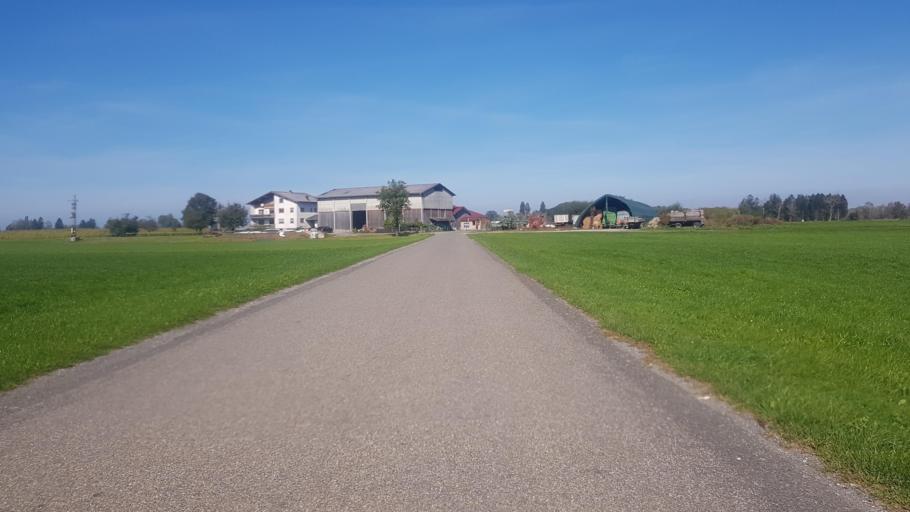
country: AT
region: Vorarlberg
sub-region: Politischer Bezirk Bregenz
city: Hochst
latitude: 47.4827
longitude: 9.6243
